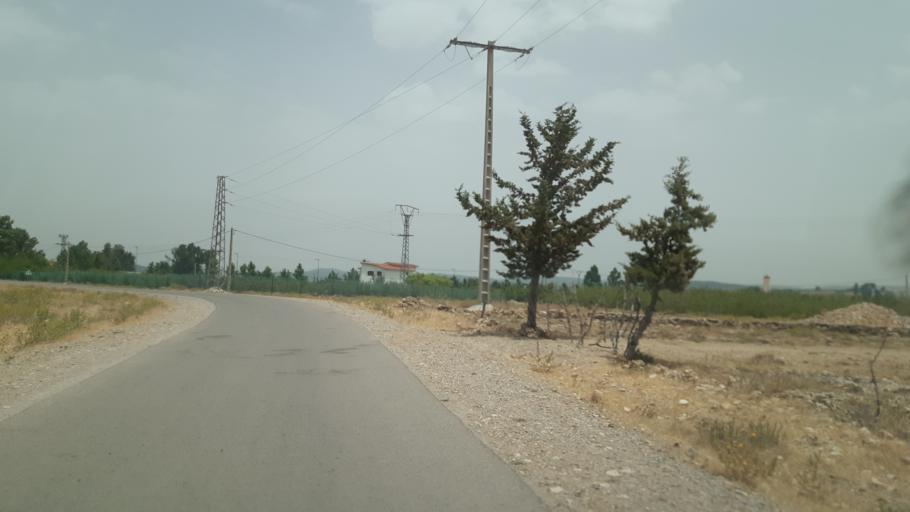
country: MA
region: Meknes-Tafilalet
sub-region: Ifrane
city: Ifrane
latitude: 33.6516
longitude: -5.0130
